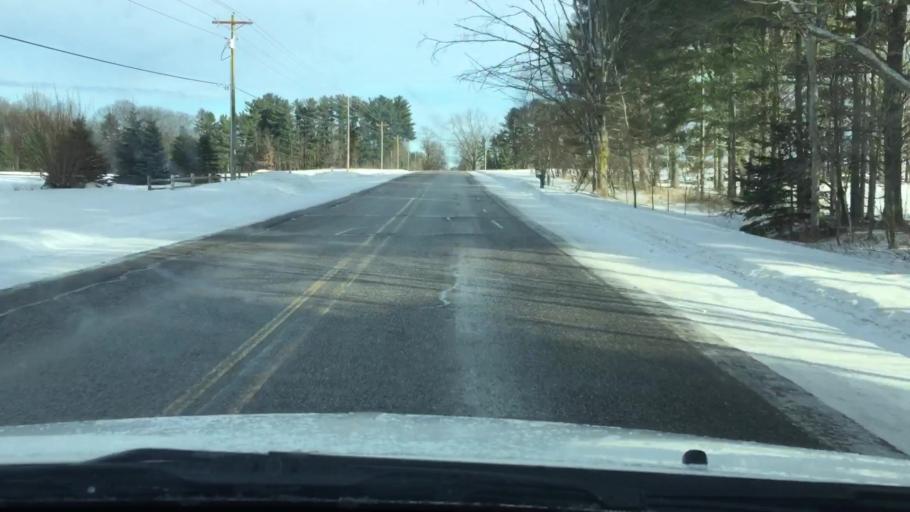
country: US
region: Michigan
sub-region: Kalkaska County
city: Kalkaska
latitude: 44.6411
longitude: -85.2622
